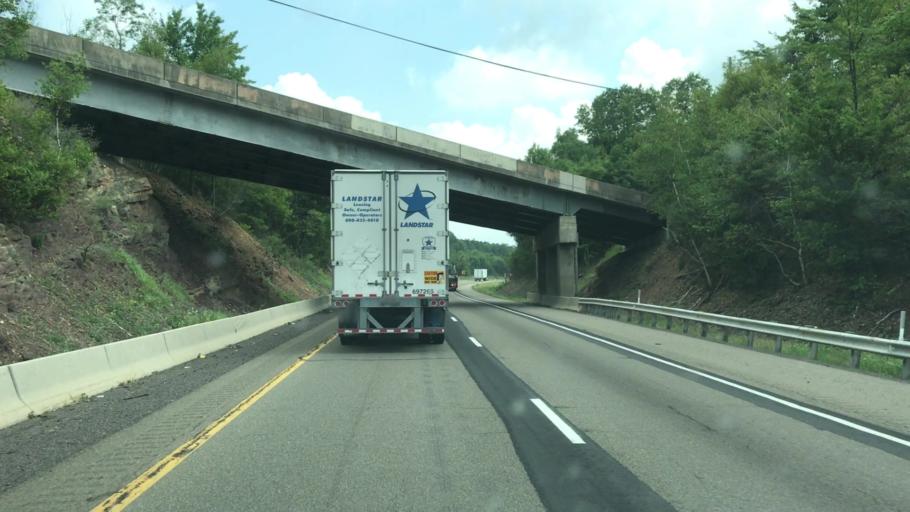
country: US
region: Pennsylvania
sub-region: Schuylkill County
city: Hometown
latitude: 40.8456
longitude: -76.0566
